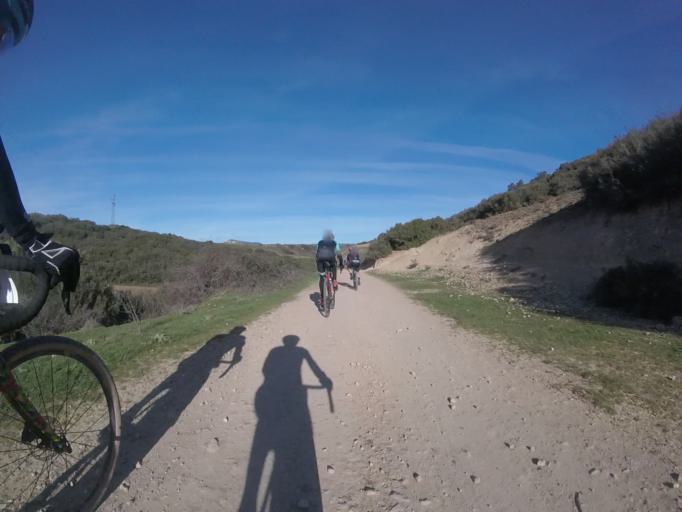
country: ES
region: Navarre
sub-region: Provincia de Navarra
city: Yerri
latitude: 42.6995
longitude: -1.9654
